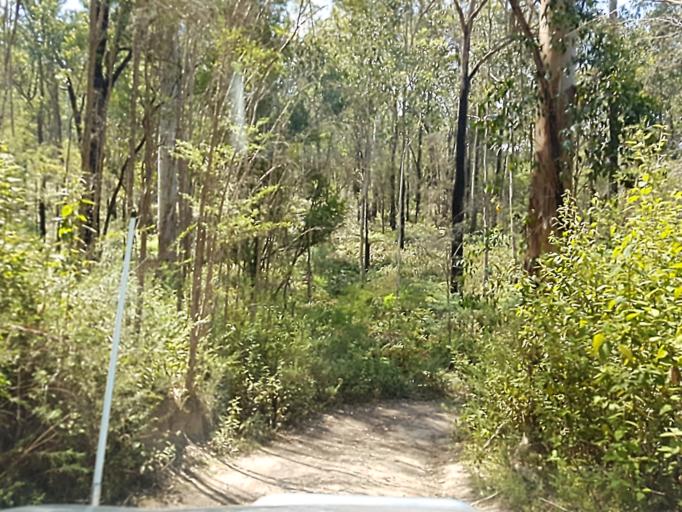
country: AU
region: Victoria
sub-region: East Gippsland
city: Lakes Entrance
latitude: -37.4075
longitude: 148.3105
